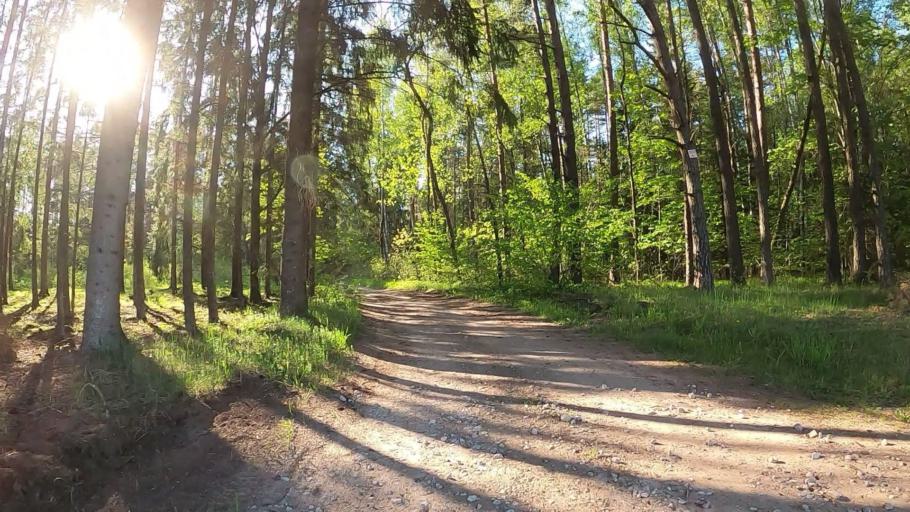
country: LV
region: Baldone
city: Baldone
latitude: 56.7657
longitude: 24.3706
